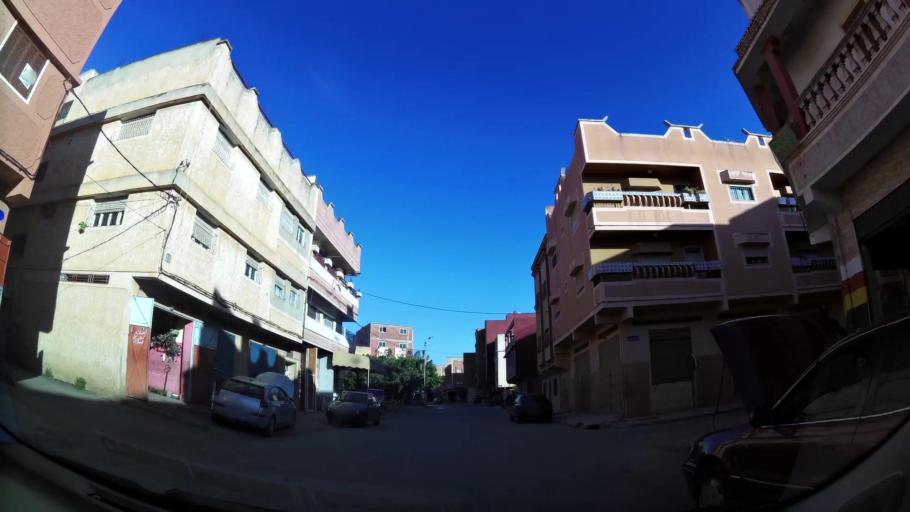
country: MA
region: Oriental
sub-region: Berkane-Taourirt
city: Berkane
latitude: 34.9311
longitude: -2.3233
